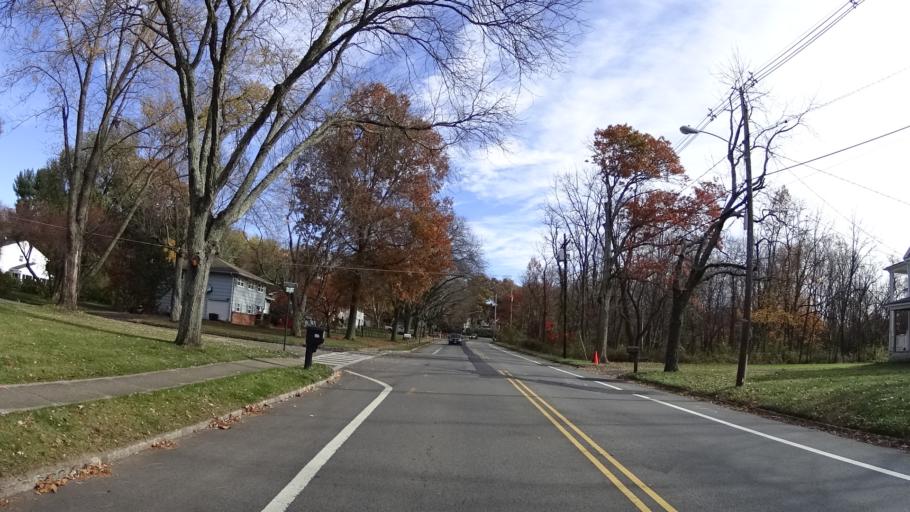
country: US
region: New Jersey
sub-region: Morris County
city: Madison
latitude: 40.7364
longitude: -74.4214
